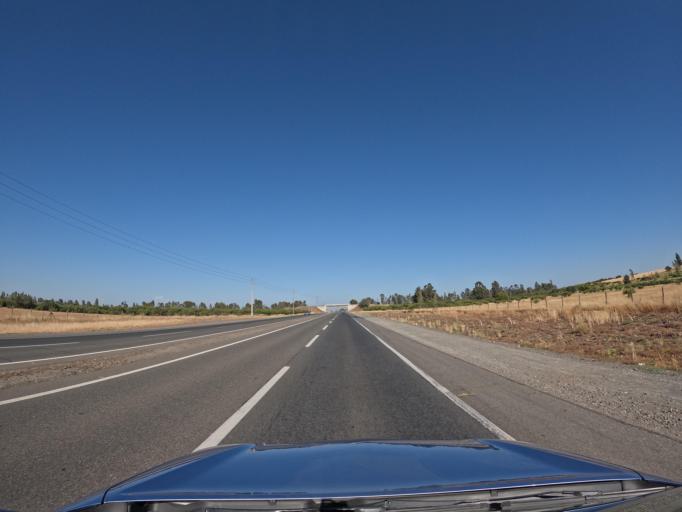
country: CL
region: Biobio
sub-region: Provincia de Nuble
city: Bulnes
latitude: -36.6589
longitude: -72.2812
